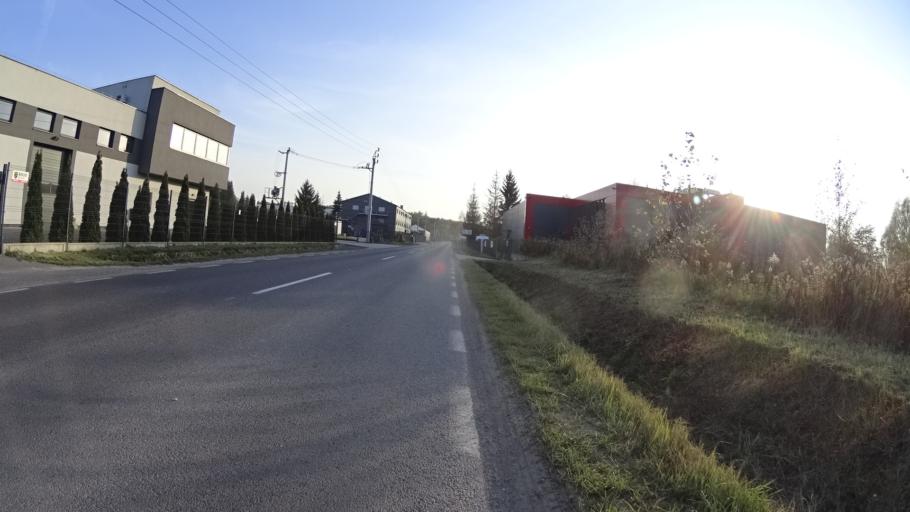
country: PL
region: Masovian Voivodeship
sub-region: Powiat warszawski zachodni
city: Babice
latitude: 52.2793
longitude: 20.8664
